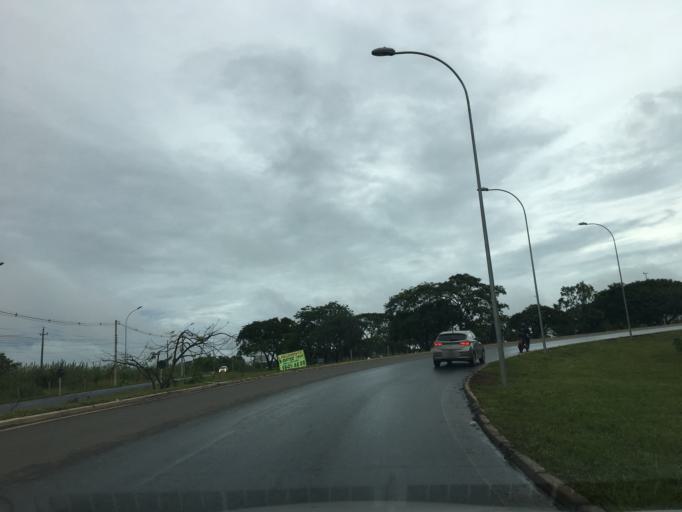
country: BR
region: Federal District
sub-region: Brasilia
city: Brasilia
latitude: -15.8415
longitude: -47.9544
